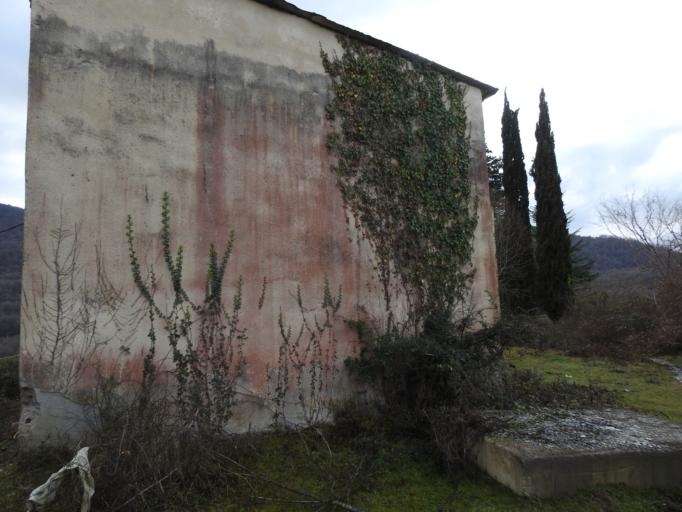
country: GE
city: Gantiadi
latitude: 43.4288
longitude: 40.1480
